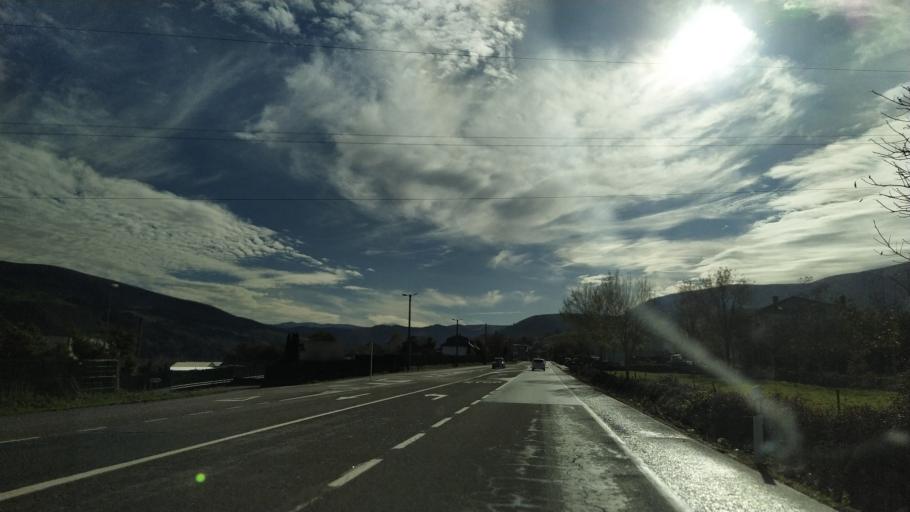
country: ES
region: Cantabria
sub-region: Provincia de Cantabria
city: Santiurde de Toranzo
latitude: 43.2162
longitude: -3.9417
